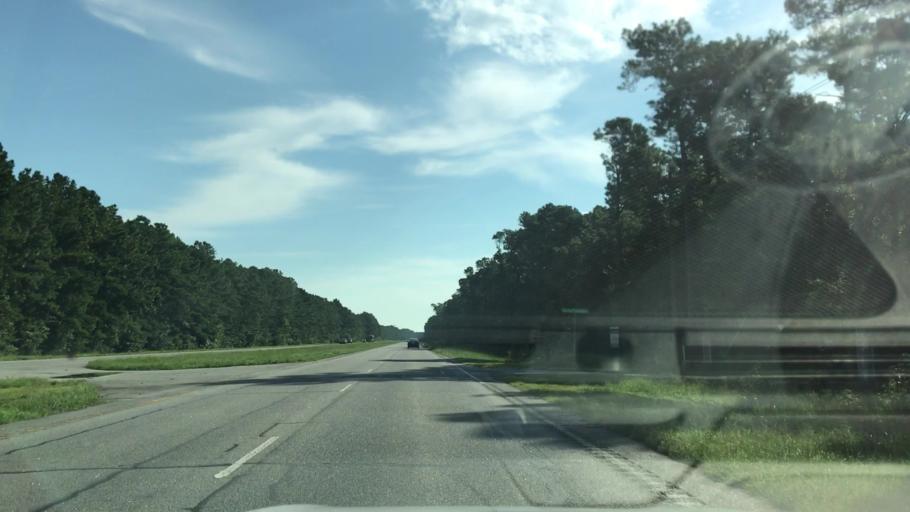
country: US
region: South Carolina
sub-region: Charleston County
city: Awendaw
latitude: 33.0641
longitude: -79.5325
